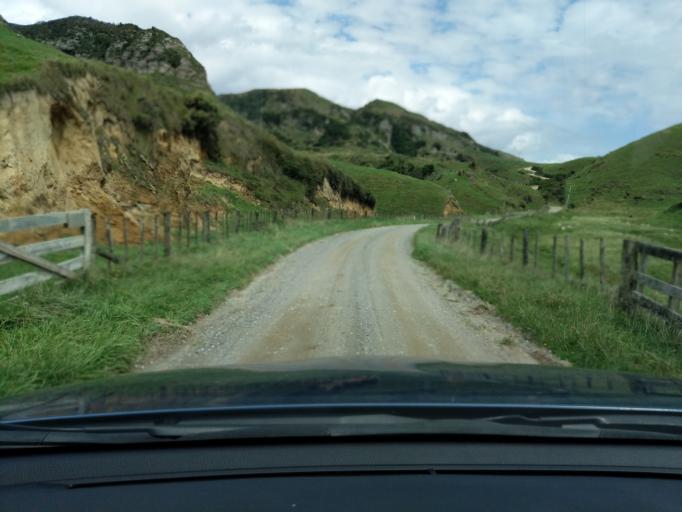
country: NZ
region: Tasman
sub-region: Tasman District
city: Takaka
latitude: -40.6552
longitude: 172.4187
